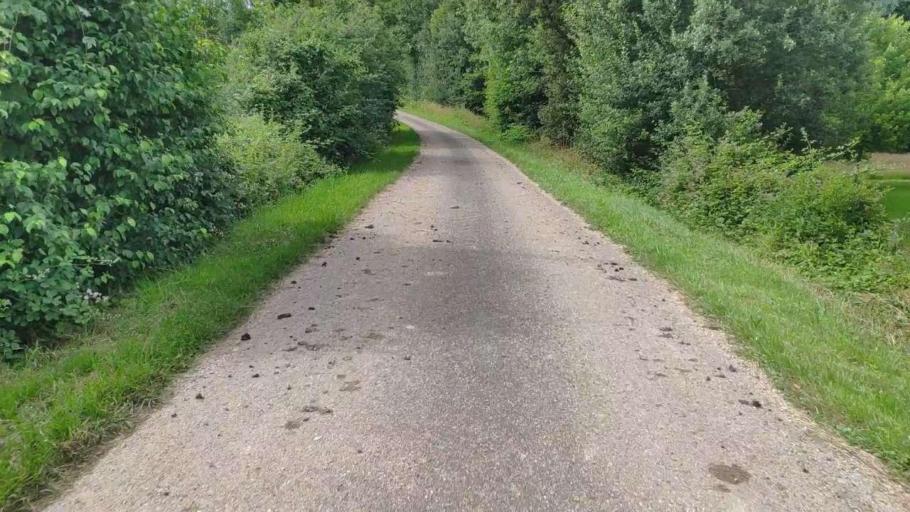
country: FR
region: Franche-Comte
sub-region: Departement du Jura
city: Bletterans
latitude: 46.7940
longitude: 5.4519
